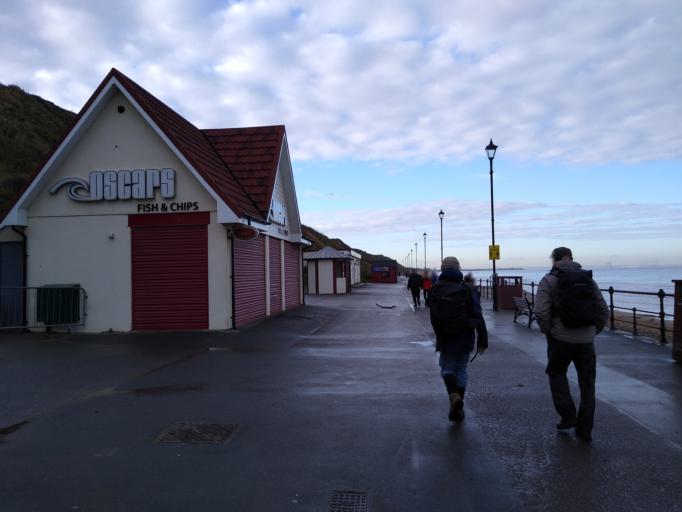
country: GB
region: England
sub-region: Redcar and Cleveland
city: Saltburn-by-the-Sea
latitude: 54.5864
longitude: -0.9717
